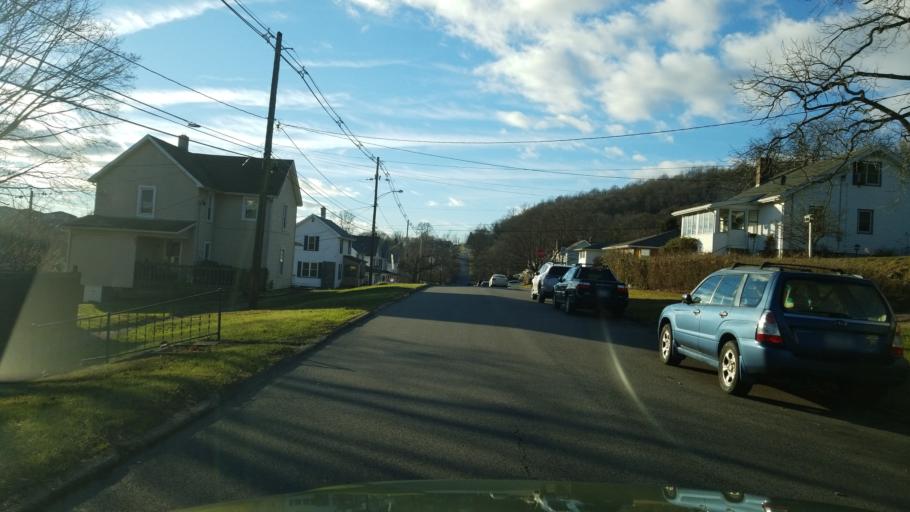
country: US
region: Pennsylvania
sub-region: Indiana County
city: Indiana
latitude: 40.6246
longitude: -79.1676
